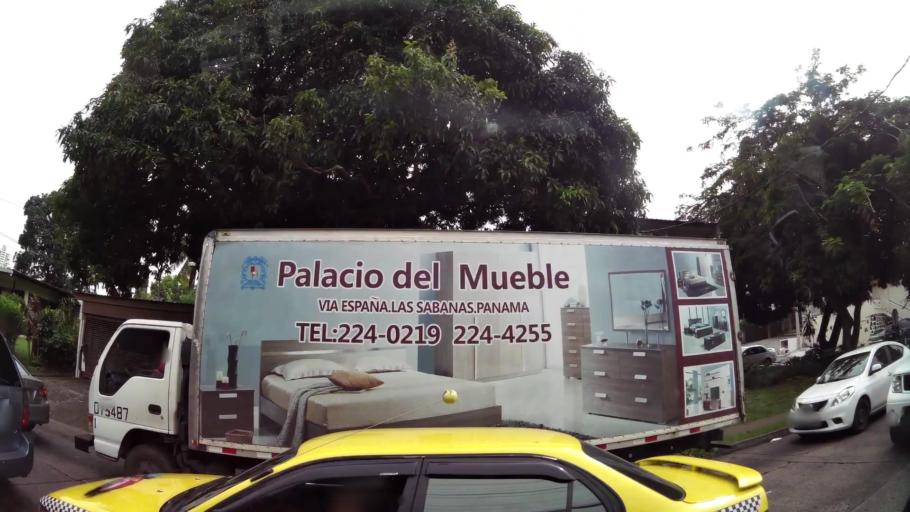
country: PA
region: Panama
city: Panama
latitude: 9.0162
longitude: -79.5196
